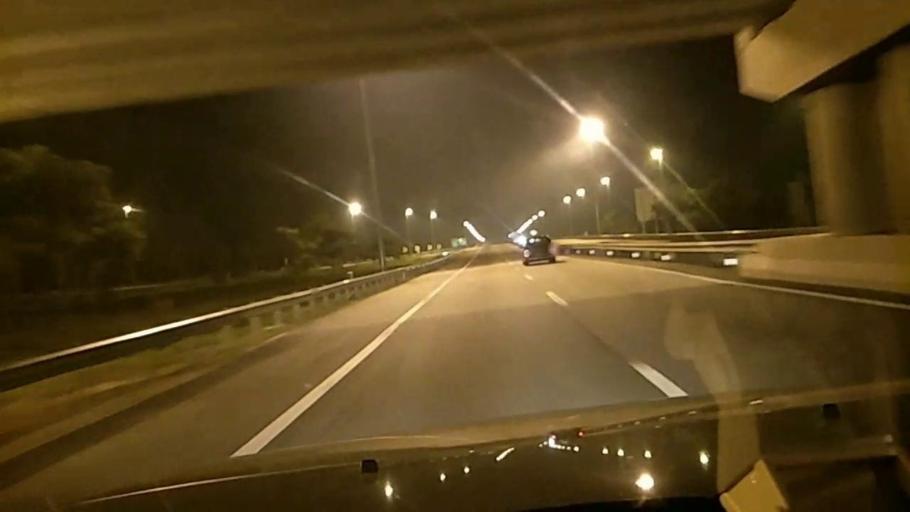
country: MY
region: Penang
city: Juru
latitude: 5.2506
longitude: 100.4702
